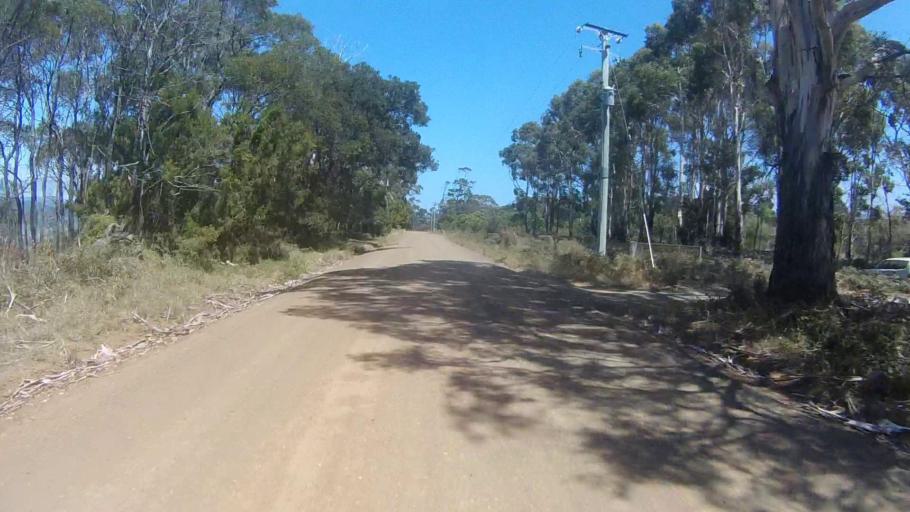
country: AU
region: Tasmania
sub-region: Sorell
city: Sorell
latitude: -42.8340
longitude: 147.8552
